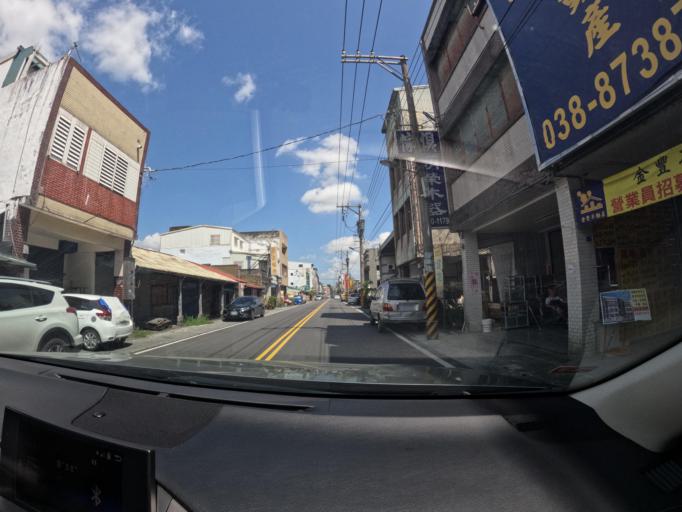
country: TW
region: Taiwan
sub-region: Hualien
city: Hualian
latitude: 23.6644
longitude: 121.4230
